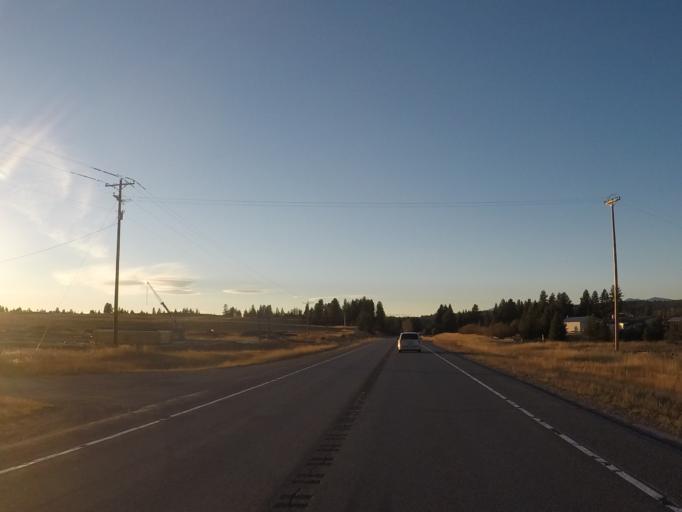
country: US
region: Montana
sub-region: Lewis and Clark County
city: Lincoln
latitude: 46.9964
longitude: -113.0277
